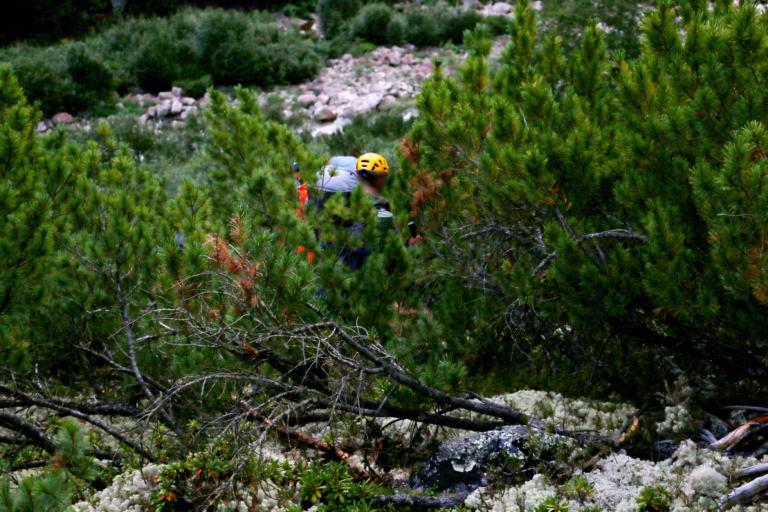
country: RU
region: Respublika Buryatiya
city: Novyy Uoyan
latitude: 56.3181
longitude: 111.2084
